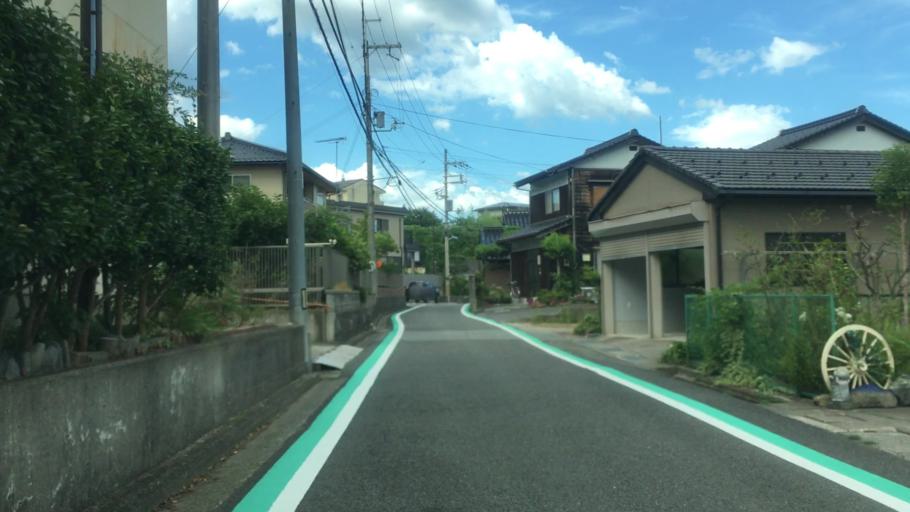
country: JP
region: Hyogo
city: Toyooka
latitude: 35.5561
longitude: 134.8057
